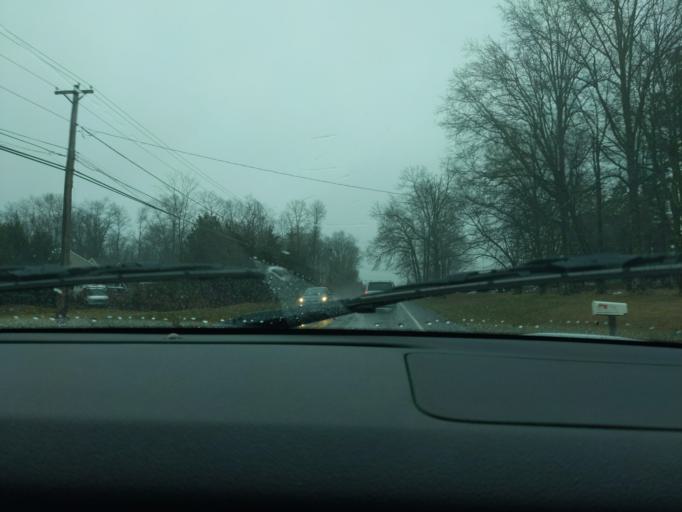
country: US
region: Pennsylvania
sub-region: Bucks County
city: Dublin
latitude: 40.3882
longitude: -75.2291
